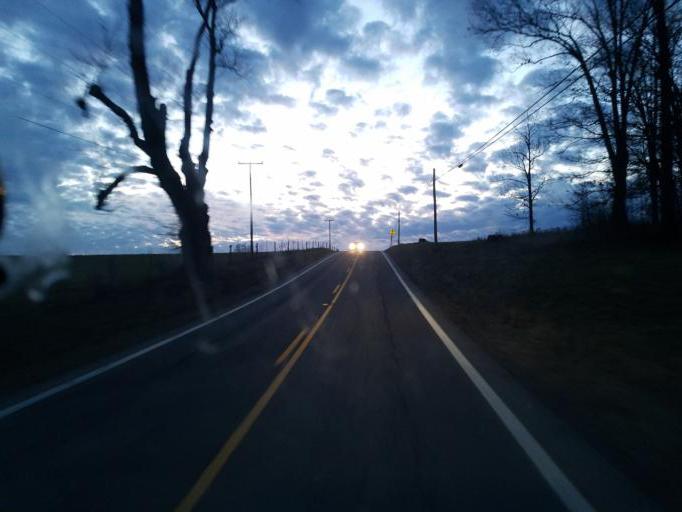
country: US
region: Ohio
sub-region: Knox County
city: Gambier
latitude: 40.2758
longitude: -82.3278
